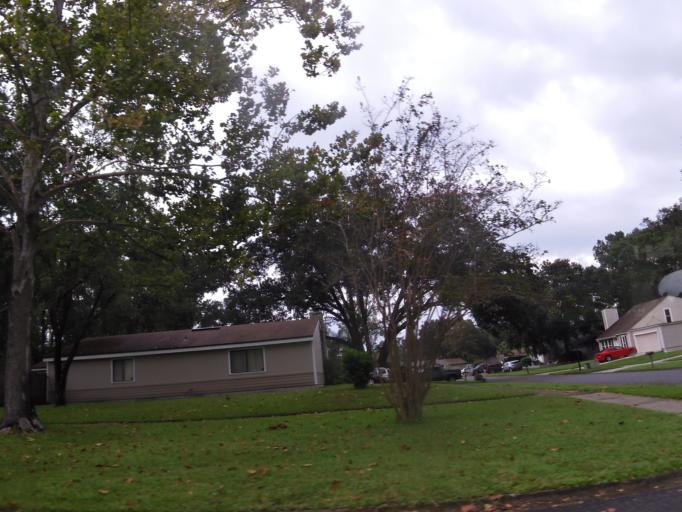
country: US
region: Florida
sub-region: Clay County
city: Bellair-Meadowbrook Terrace
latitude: 30.1914
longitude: -81.7638
